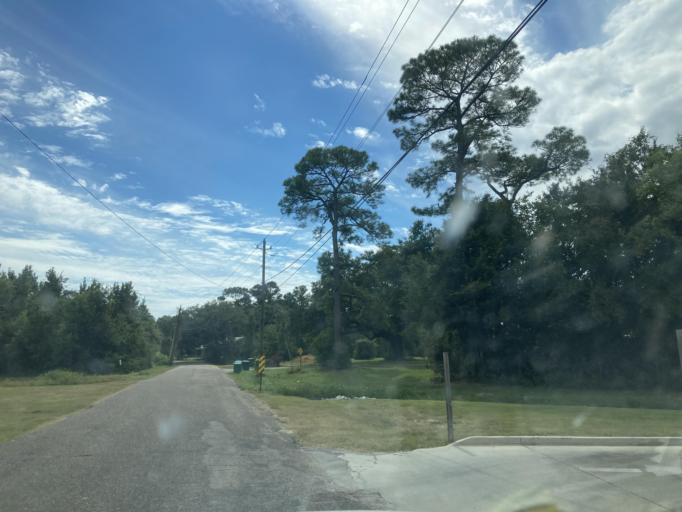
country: US
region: Mississippi
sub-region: Jackson County
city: Saint Martin
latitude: 30.4408
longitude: -88.8780
